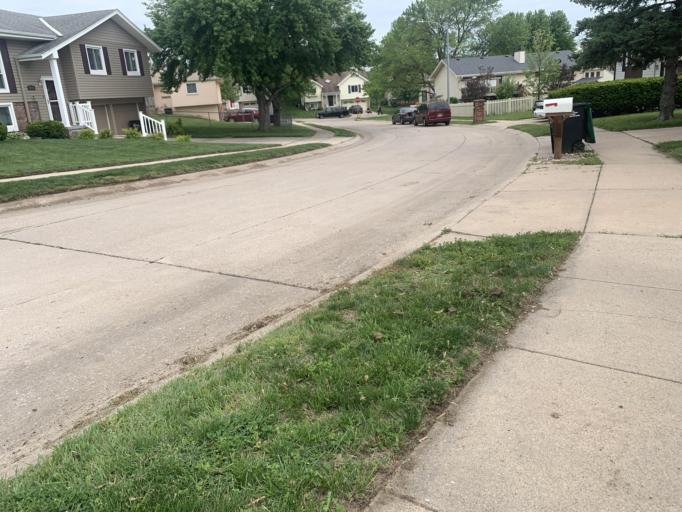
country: US
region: Nebraska
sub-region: Douglas County
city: Ralston
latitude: 41.1921
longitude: -96.0853
